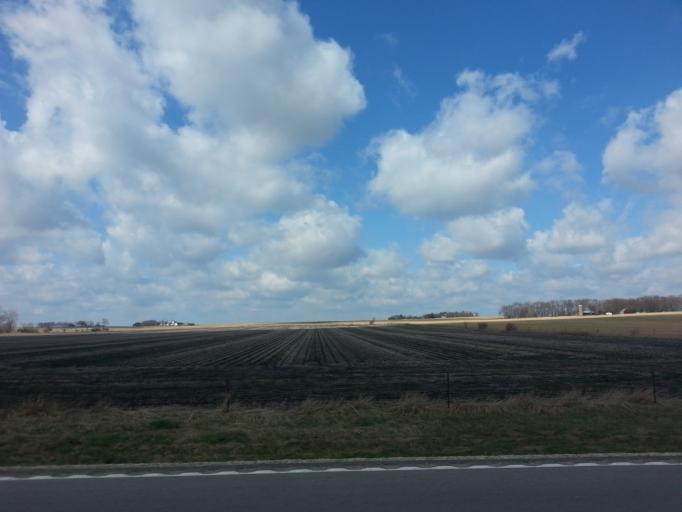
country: US
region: Minnesota
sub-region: Dodge County
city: Dodge Center
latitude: 44.0841
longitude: -92.8347
